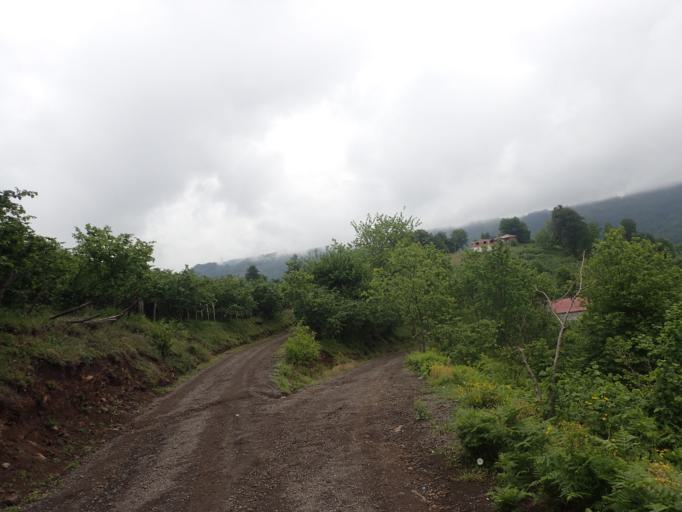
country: TR
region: Samsun
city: Salipazari
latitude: 40.9508
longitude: 36.8767
